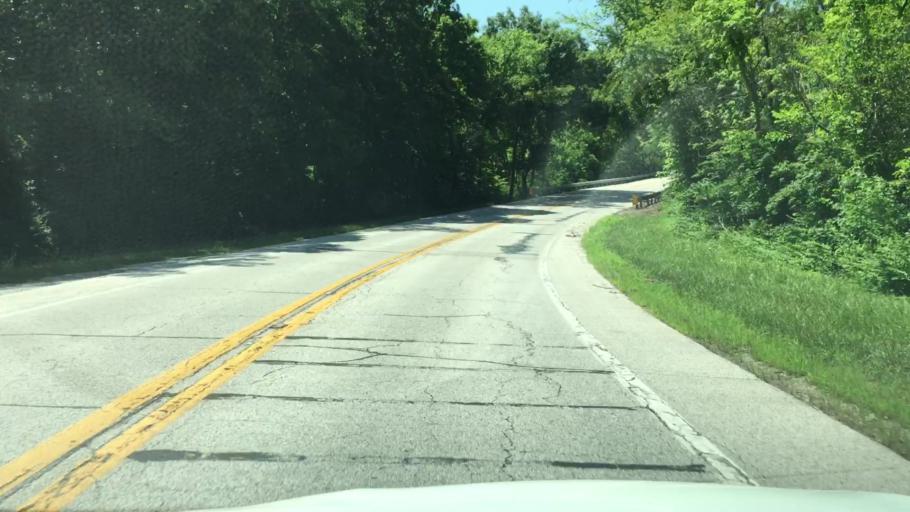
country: US
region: Illinois
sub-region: Hancock County
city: Nauvoo
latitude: 40.5176
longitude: -91.3589
